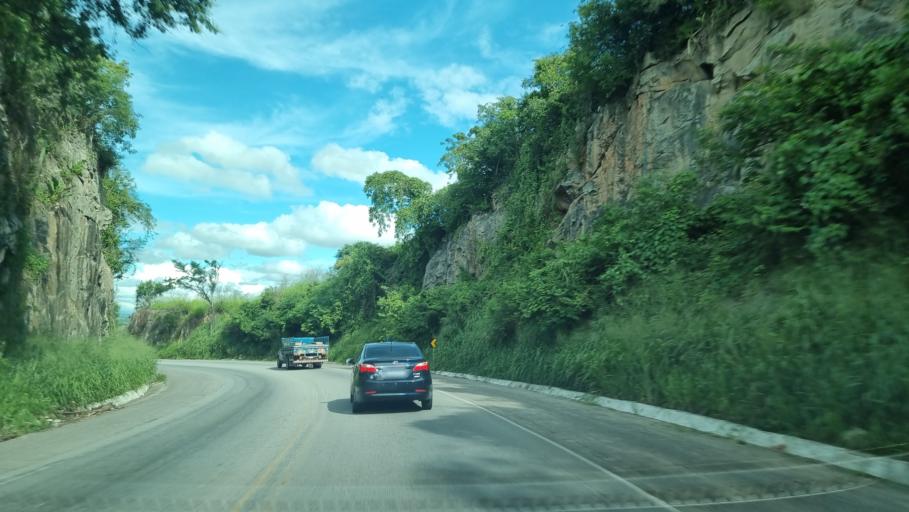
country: BR
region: Pernambuco
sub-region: Agrestina
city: Agrestina
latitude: -8.3852
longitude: -35.9823
